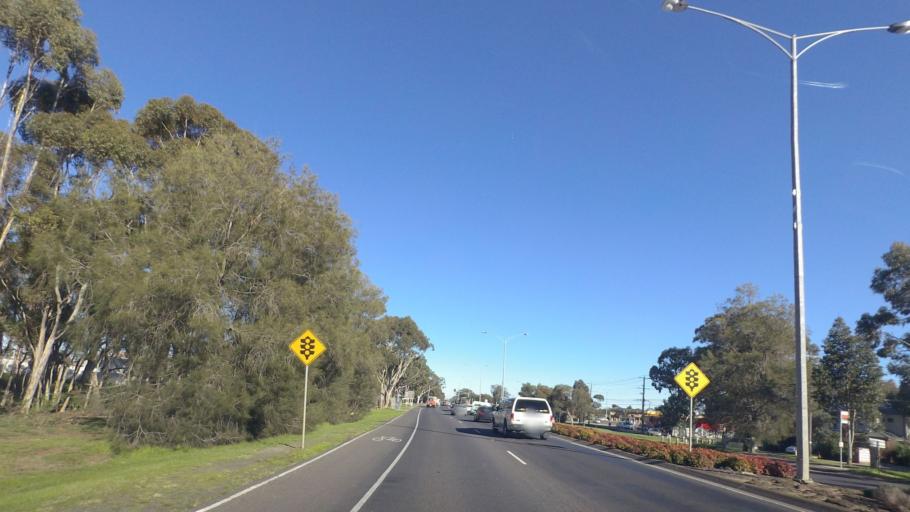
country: AU
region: Victoria
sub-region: Wyndham
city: Werribee
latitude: -37.8931
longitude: 144.6825
